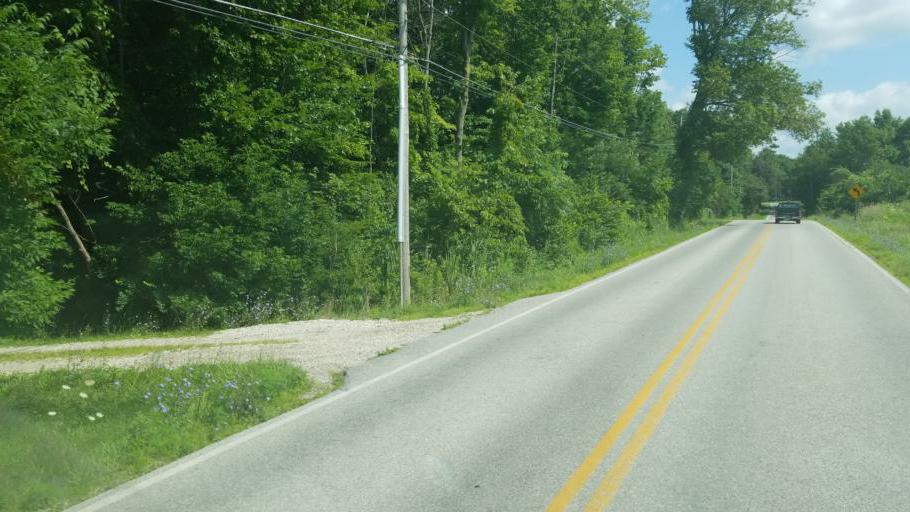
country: US
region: Ohio
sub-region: Delaware County
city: Sunbury
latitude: 40.2776
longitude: -82.9374
